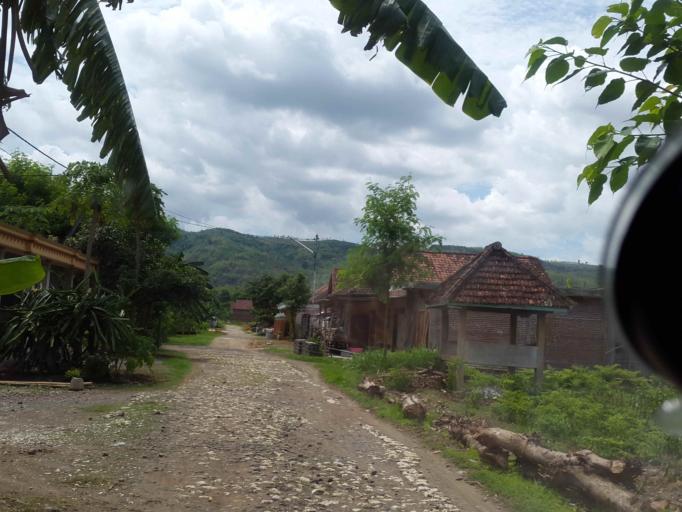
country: ID
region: East Java
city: Pelem
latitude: -8.1539
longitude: 111.8744
